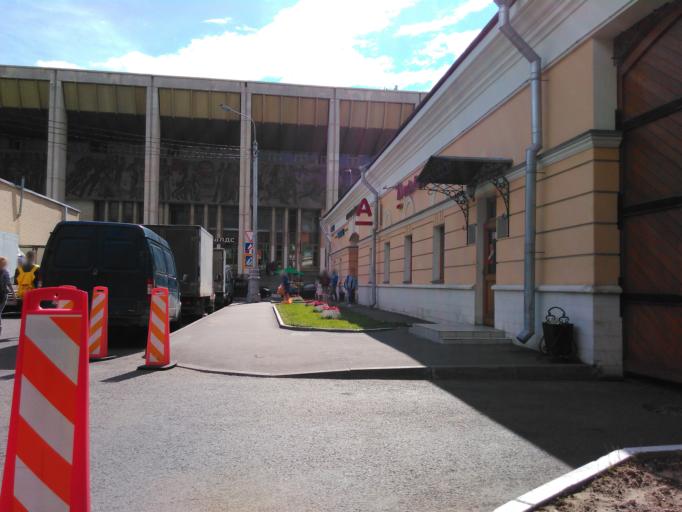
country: RU
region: Moskovskaya
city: Dorogomilovo
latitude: 55.7279
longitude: 37.5812
